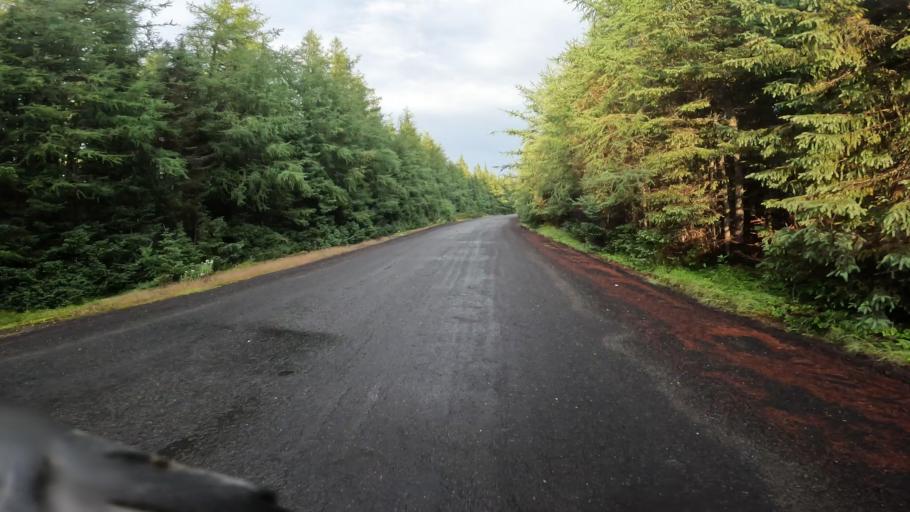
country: CA
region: Quebec
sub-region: Capitale-Nationale
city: Beaupre
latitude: 47.6388
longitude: -71.2284
